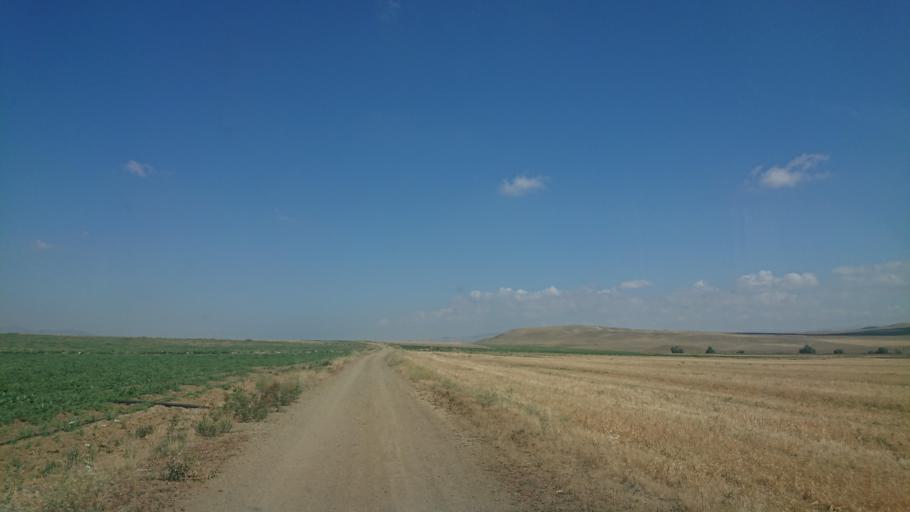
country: TR
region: Aksaray
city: Sariyahsi
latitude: 38.9645
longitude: 33.9257
